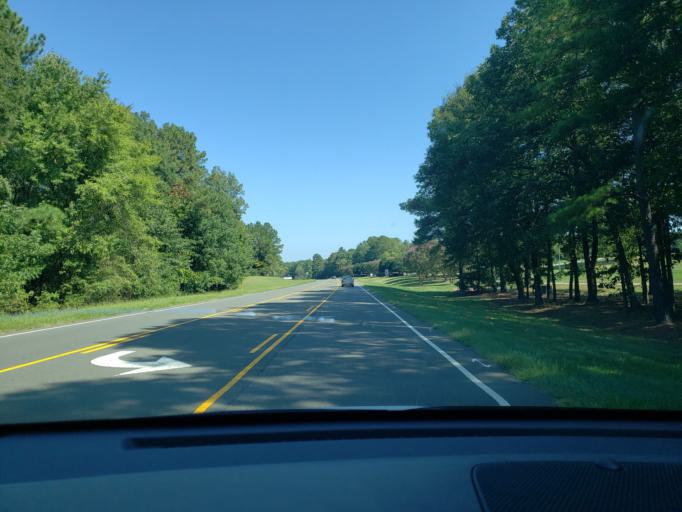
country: US
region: North Carolina
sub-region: Durham County
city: Durham
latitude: 35.9045
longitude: -78.8787
